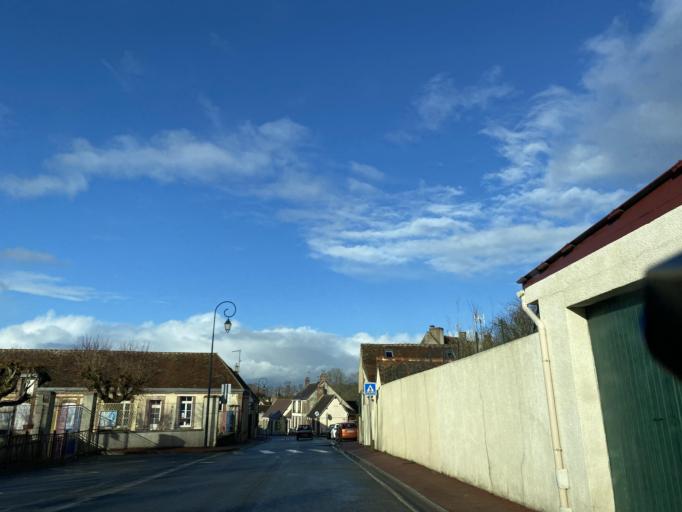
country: FR
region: Centre
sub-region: Departement d'Eure-et-Loir
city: Brezolles
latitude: 48.6281
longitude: 1.1492
